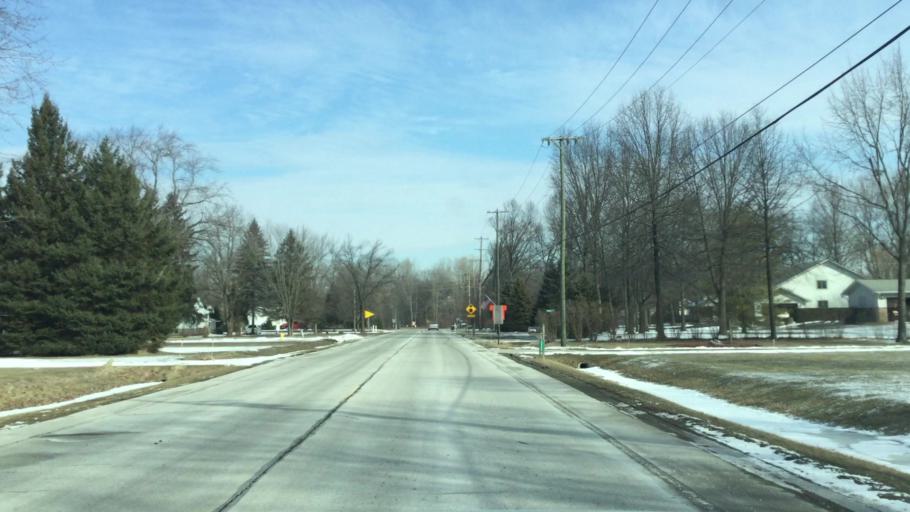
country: US
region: Michigan
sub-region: Wayne County
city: Flat Rock
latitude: 42.1354
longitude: -83.2900
